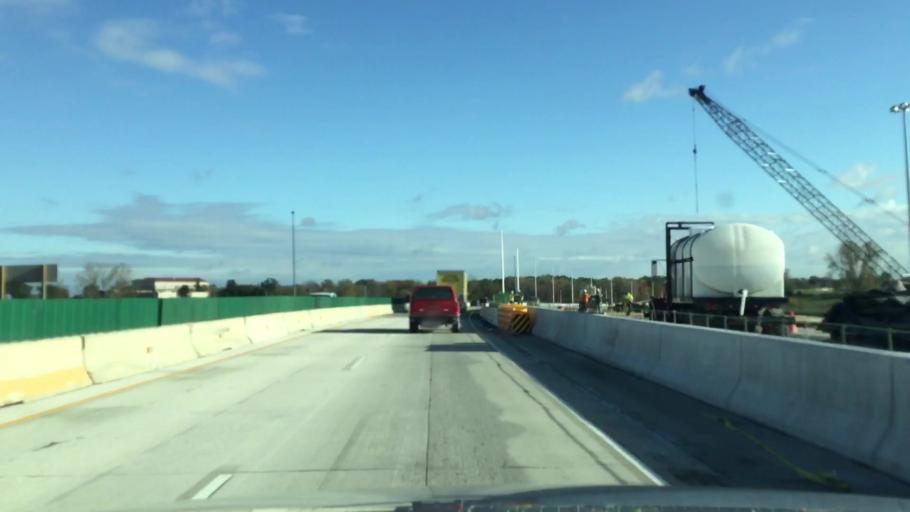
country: US
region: Michigan
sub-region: Genesee County
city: Flint
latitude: 42.9965
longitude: -83.7065
